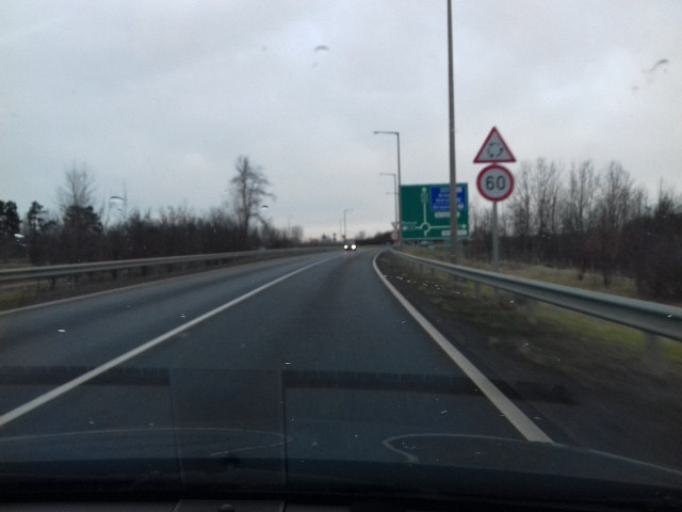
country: HU
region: Szabolcs-Szatmar-Bereg
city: Nyirpazony
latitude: 47.9526
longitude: 21.8205
